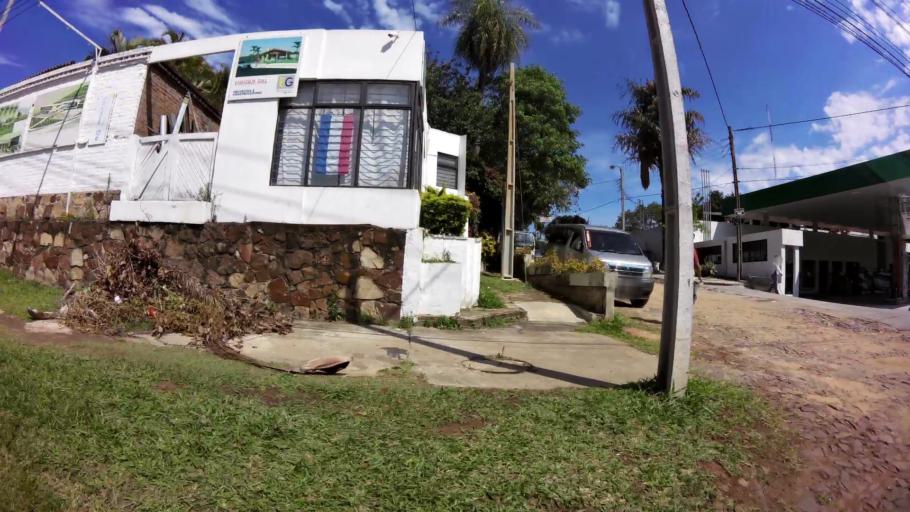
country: PY
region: Central
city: San Lorenzo
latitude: -25.2746
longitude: -57.4965
